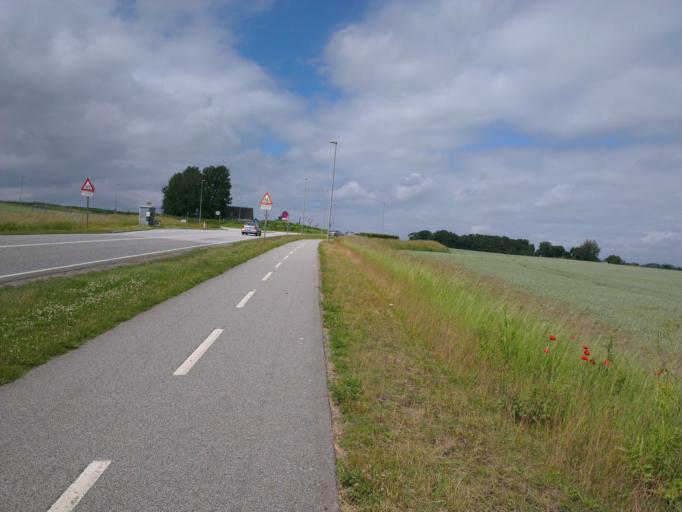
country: DK
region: Zealand
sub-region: Lejre Kommune
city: Lejre
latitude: 55.6551
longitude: 11.9209
